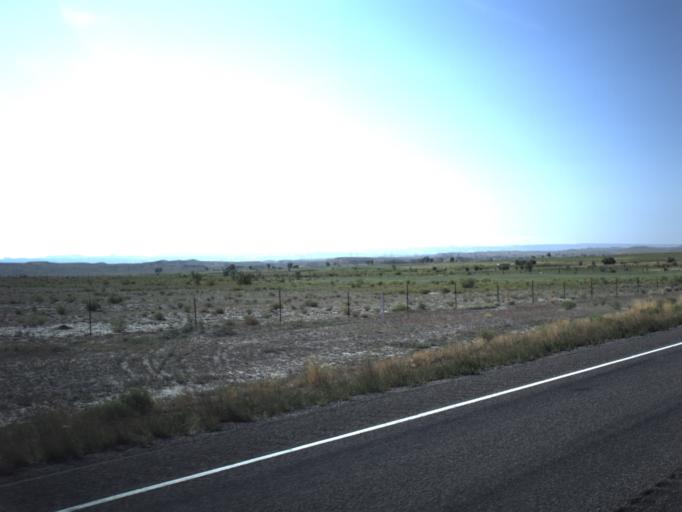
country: US
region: Utah
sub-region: Emery County
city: Castle Dale
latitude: 39.2377
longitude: -110.9913
